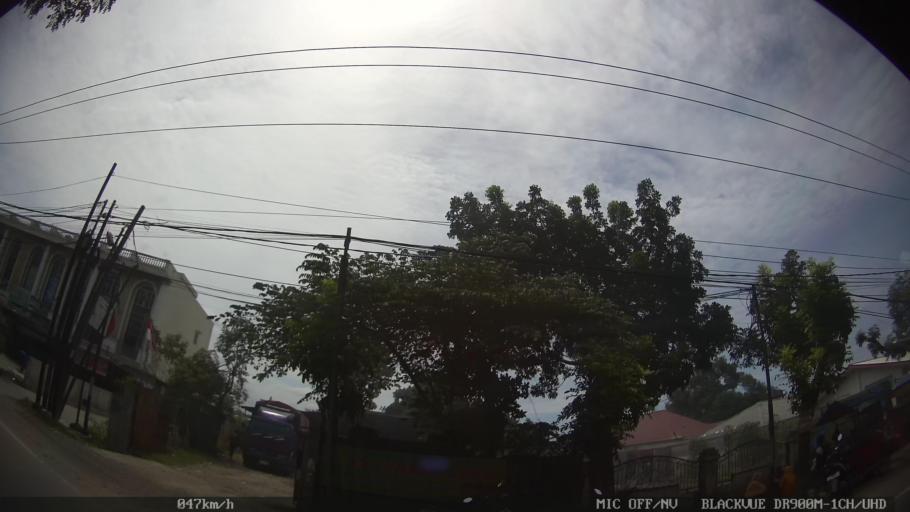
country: ID
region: North Sumatra
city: Sunggal
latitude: 3.5781
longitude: 98.6132
